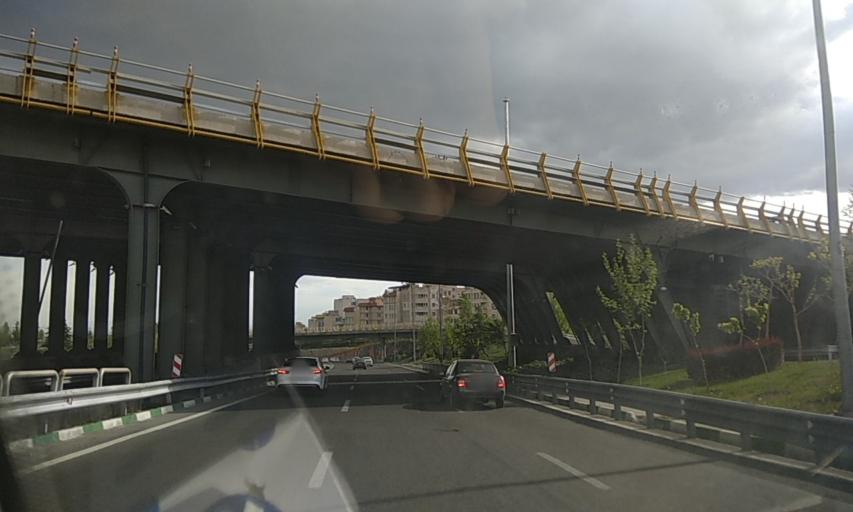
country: IR
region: Tehran
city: Tajrish
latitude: 35.7640
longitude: 51.2969
